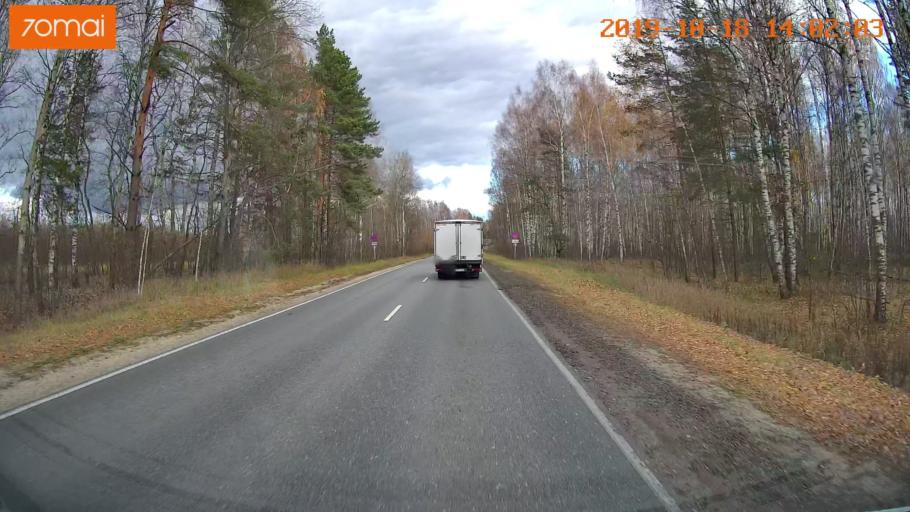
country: RU
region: Rjazan
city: Spas-Klepiki
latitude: 55.1110
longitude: 40.1006
